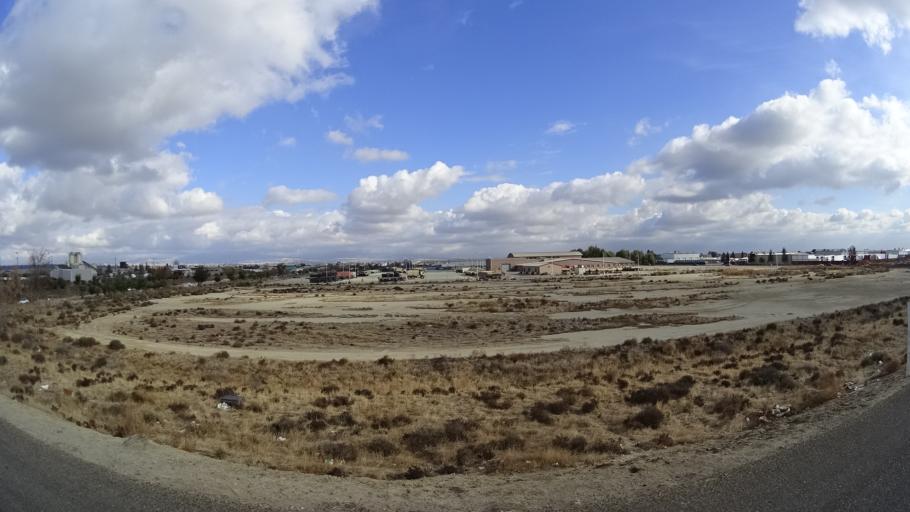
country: US
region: California
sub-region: Kern County
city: Bakersfield
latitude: 35.3515
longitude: -118.9766
